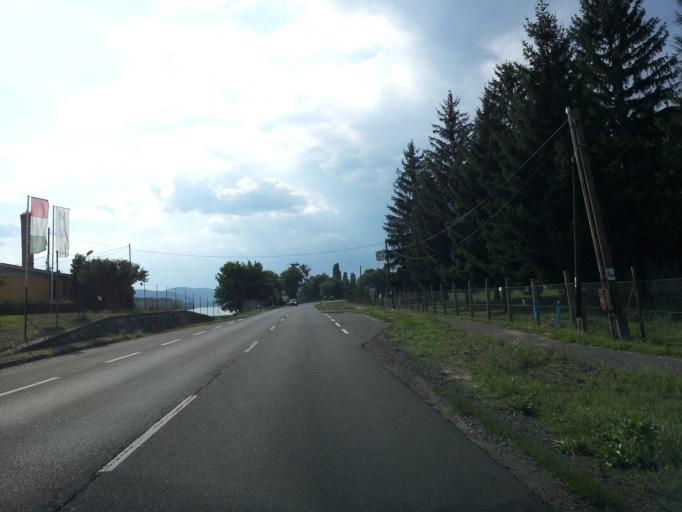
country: HU
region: Pest
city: Veroce
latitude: 47.8182
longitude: 19.0549
